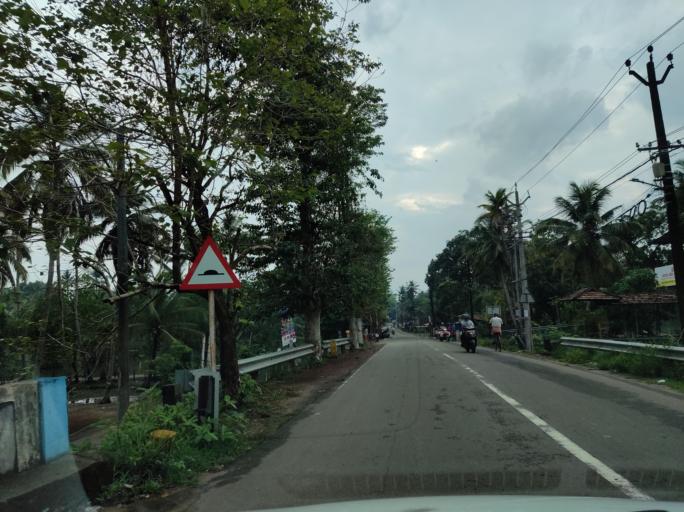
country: IN
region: Kerala
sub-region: Alappuzha
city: Kayankulam
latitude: 9.2586
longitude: 76.4329
